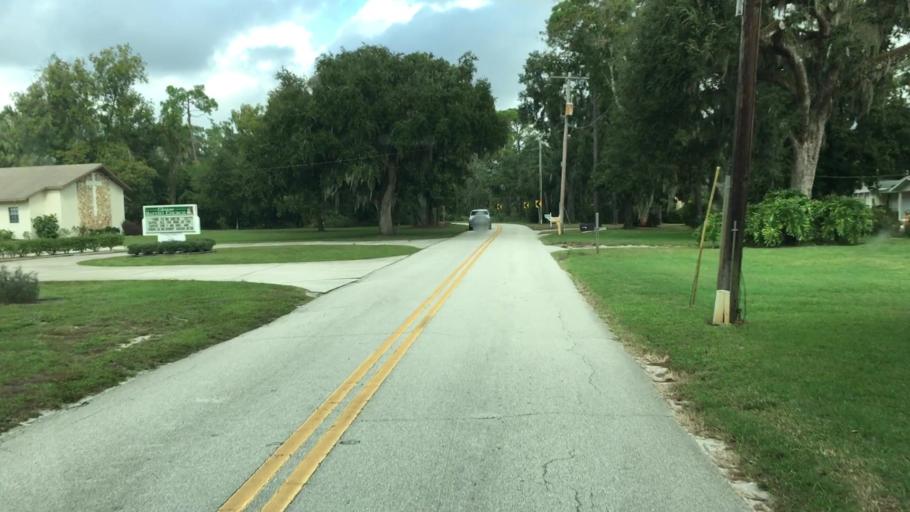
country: US
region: Florida
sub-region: Volusia County
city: Glencoe
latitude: 29.0150
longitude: -80.9706
